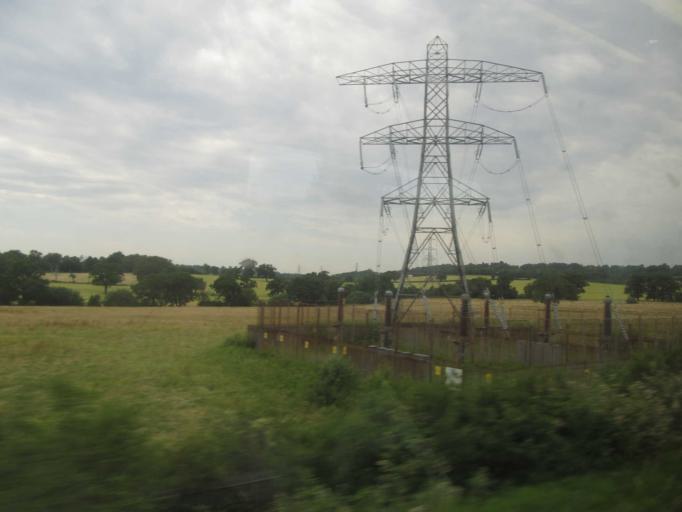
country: GB
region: England
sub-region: Greater London
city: Edgware
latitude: 51.6330
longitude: -0.2679
